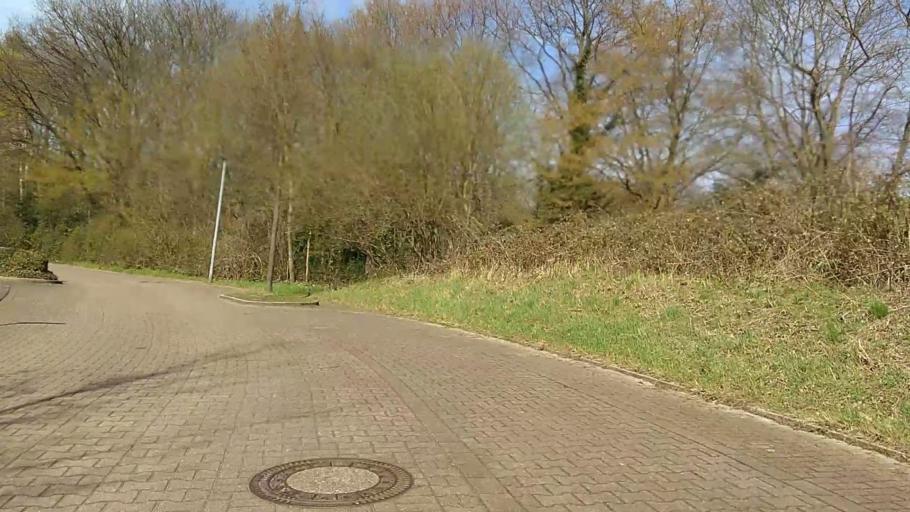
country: DE
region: North Rhine-Westphalia
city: Herten
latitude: 51.5751
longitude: 7.0853
